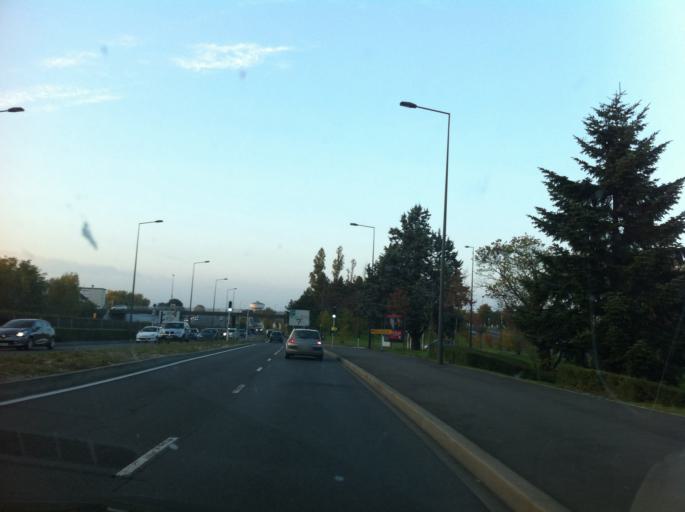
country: FR
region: Centre
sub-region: Departement d'Indre-et-Loire
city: Saint-Avertin
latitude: 47.3754
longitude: 0.7202
